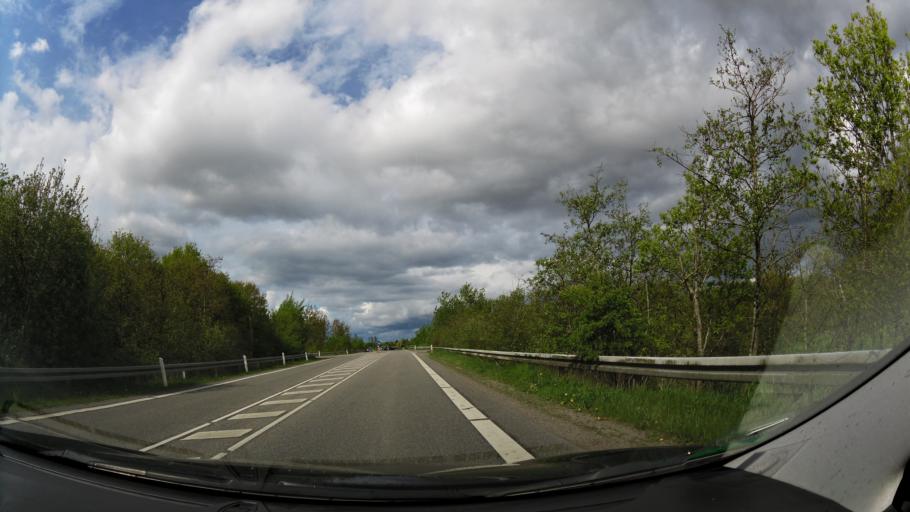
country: DK
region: South Denmark
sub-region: Nyborg Kommune
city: Nyborg
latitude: 55.3303
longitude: 10.7405
